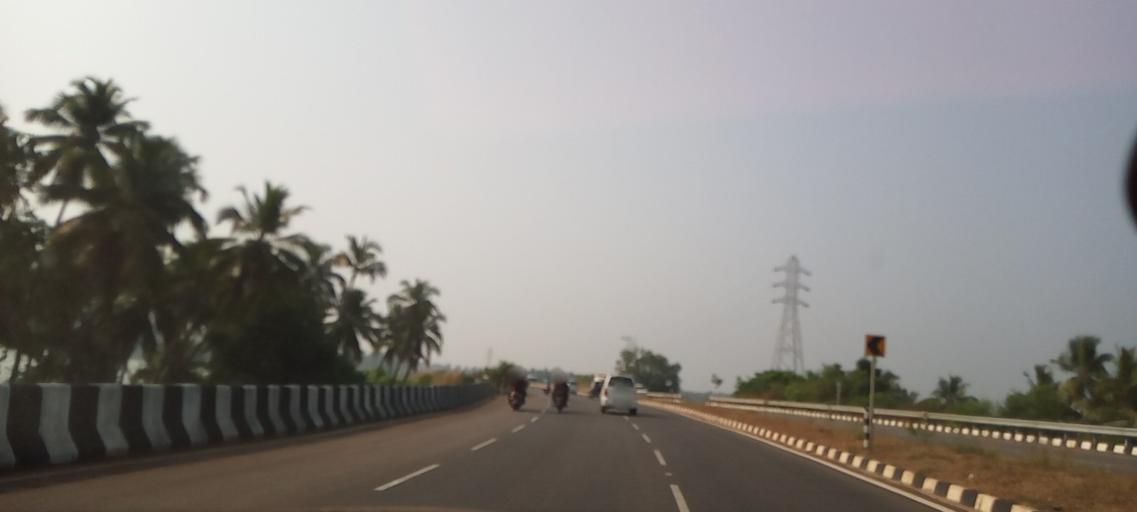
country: IN
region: Karnataka
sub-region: Udupi
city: Coondapoor
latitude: 13.6426
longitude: 74.7014
